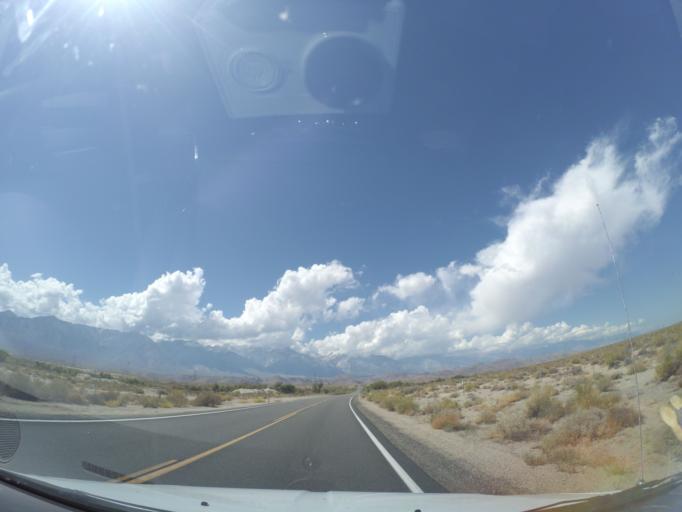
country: US
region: California
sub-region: Inyo County
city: Lone Pine
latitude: 36.5743
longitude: -118.0087
